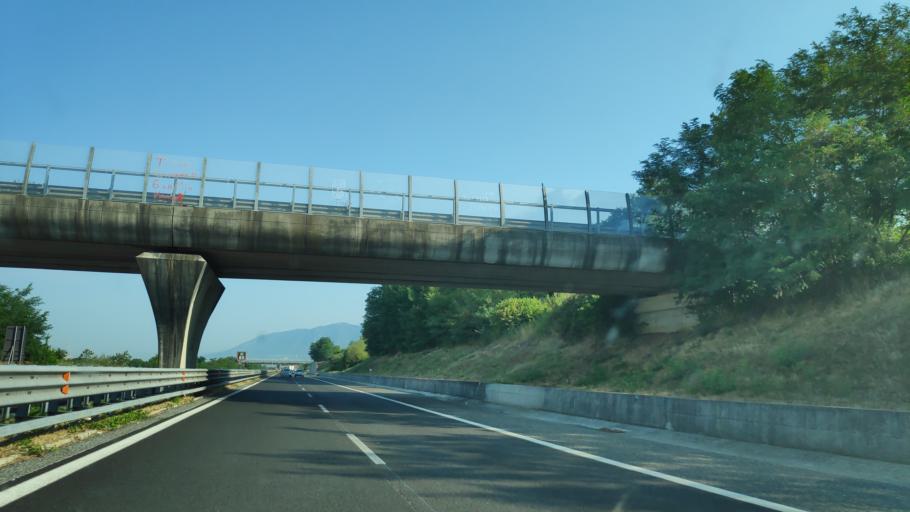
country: IT
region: Campania
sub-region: Provincia di Salerno
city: Buonabitacolo
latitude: 40.2776
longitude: 15.6541
